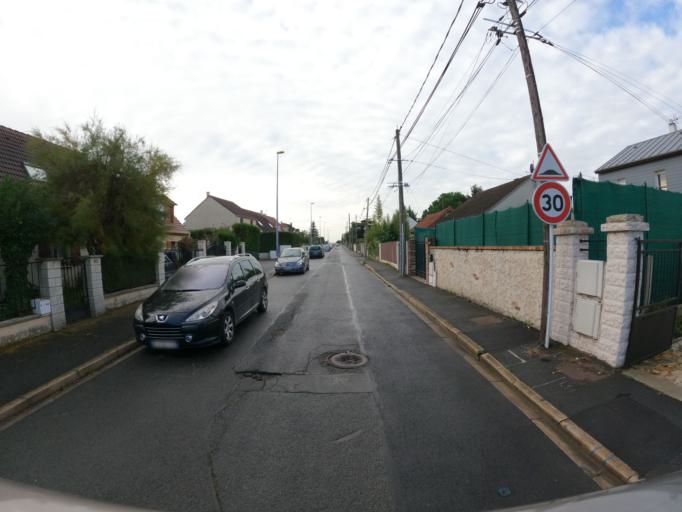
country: FR
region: Ile-de-France
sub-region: Departement de Seine-et-Marne
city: Courtry
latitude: 48.9018
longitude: 2.6087
